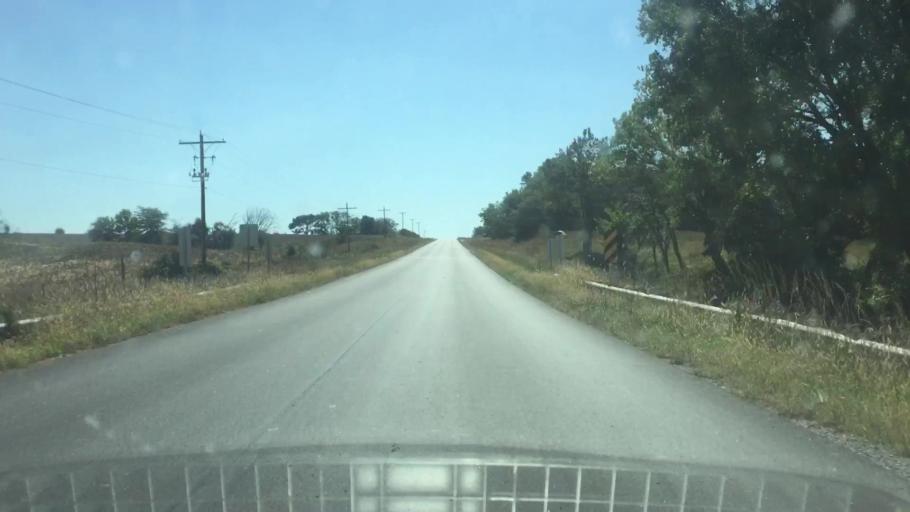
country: US
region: Kansas
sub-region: Marshall County
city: Marysville
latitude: 39.9379
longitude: -96.6009
